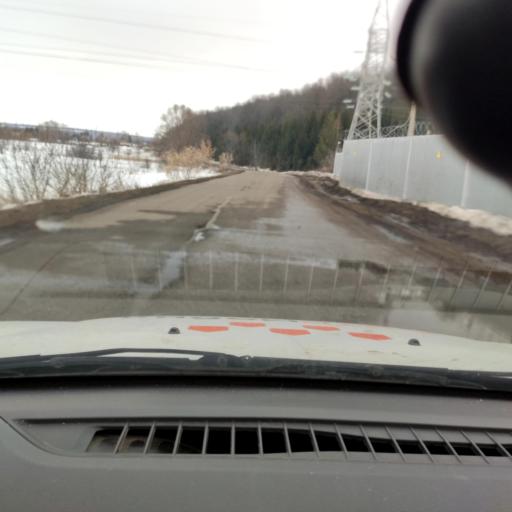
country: RU
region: Bashkortostan
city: Ufa
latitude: 54.5311
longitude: 55.9127
